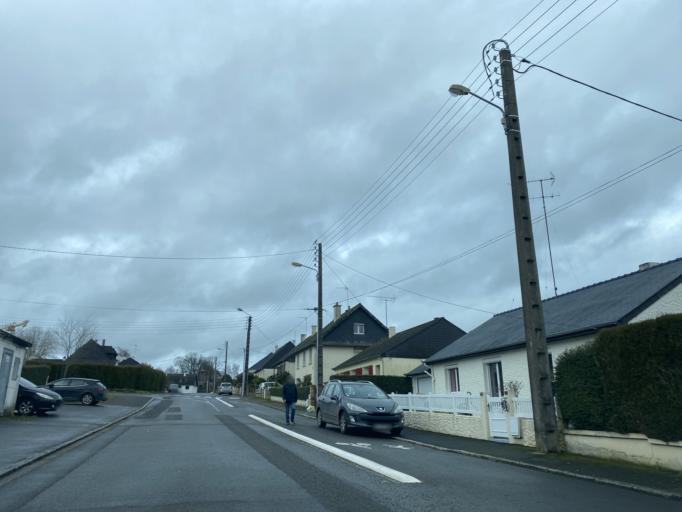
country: FR
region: Brittany
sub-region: Departement d'Ille-et-Vilaine
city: Melesse
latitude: 48.2158
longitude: -1.6925
